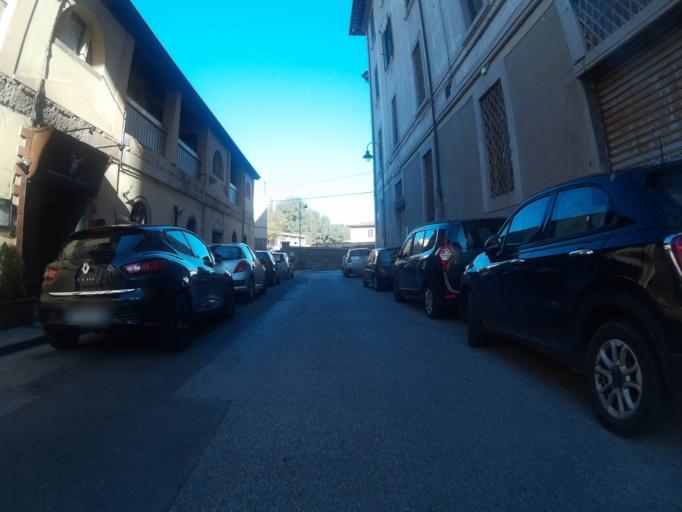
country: IT
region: Tuscany
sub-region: Provincia di Livorno
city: Livorno
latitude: 43.5556
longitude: 10.3082
